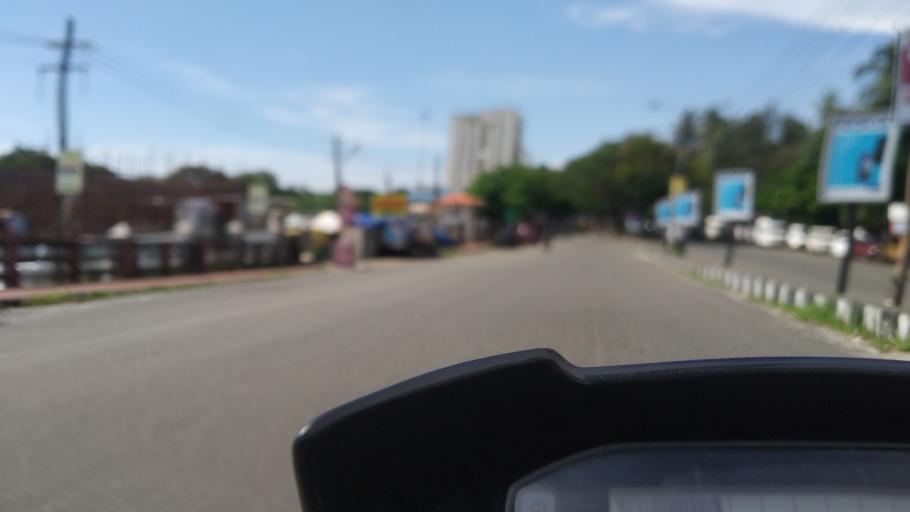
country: IN
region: Kerala
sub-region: Ernakulam
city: Cochin
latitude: 9.9806
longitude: 76.2756
